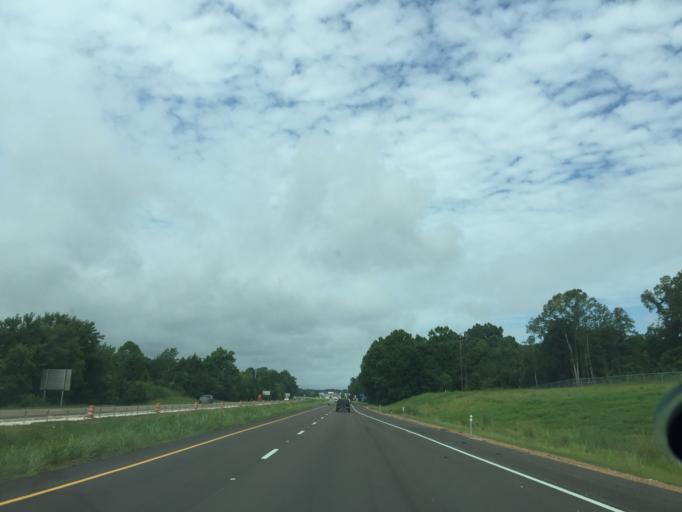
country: US
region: Mississippi
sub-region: Rankin County
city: Brandon
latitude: 32.2800
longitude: -90.0120
